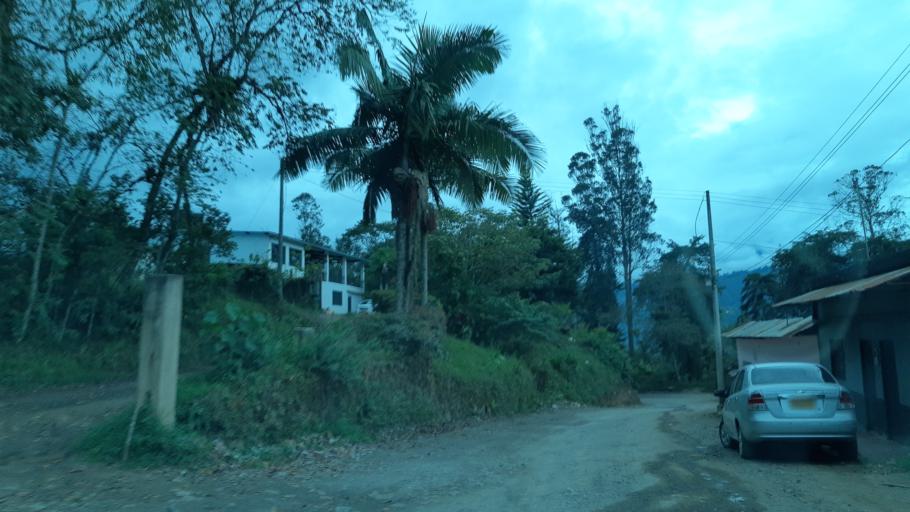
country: CO
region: Boyaca
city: Garagoa
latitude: 5.0855
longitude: -73.3558
